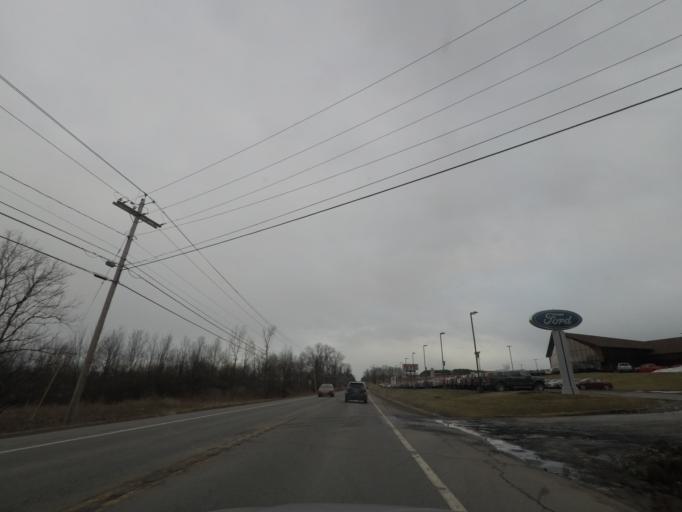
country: US
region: New York
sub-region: Madison County
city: Wampsville
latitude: 43.0765
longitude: -75.6855
